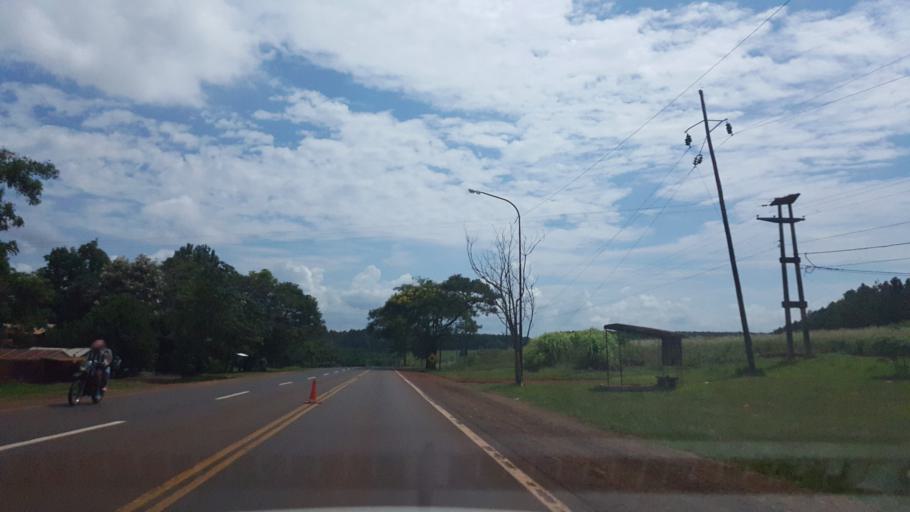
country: AR
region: Misiones
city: Capiovi
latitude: -26.9098
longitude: -55.0606
